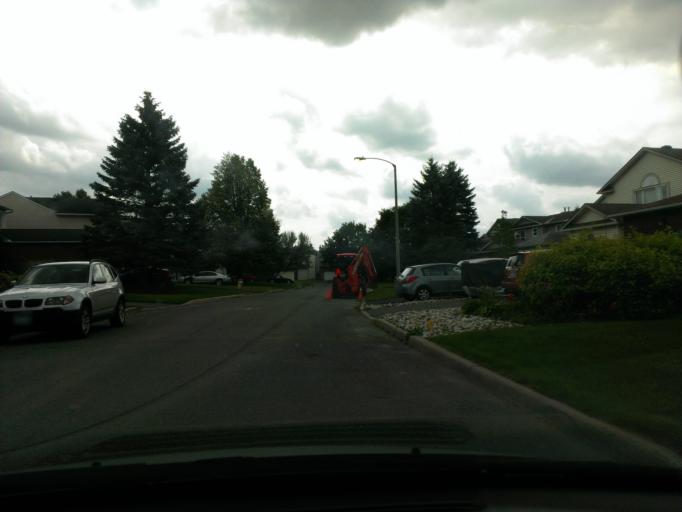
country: CA
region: Ontario
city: Clarence-Rockland
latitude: 45.4846
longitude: -75.4891
